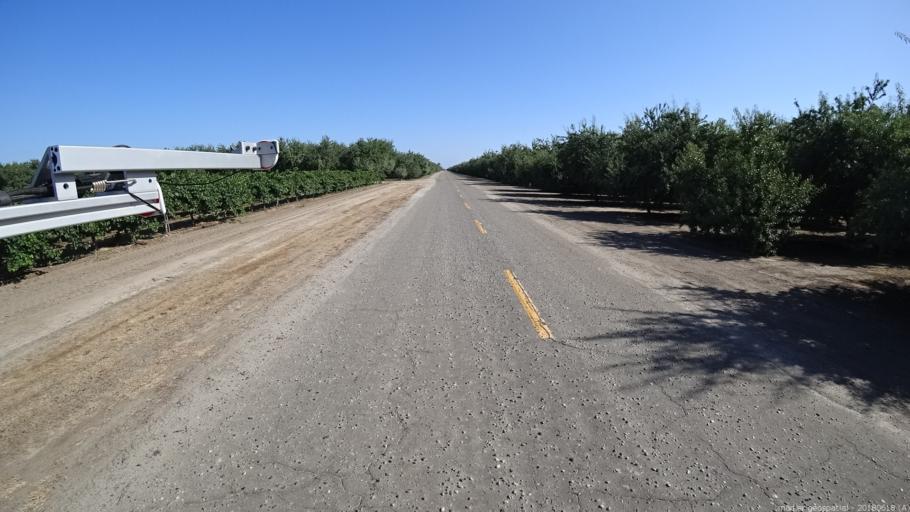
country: US
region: California
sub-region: Madera County
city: Parkwood
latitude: 36.8980
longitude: -120.1377
